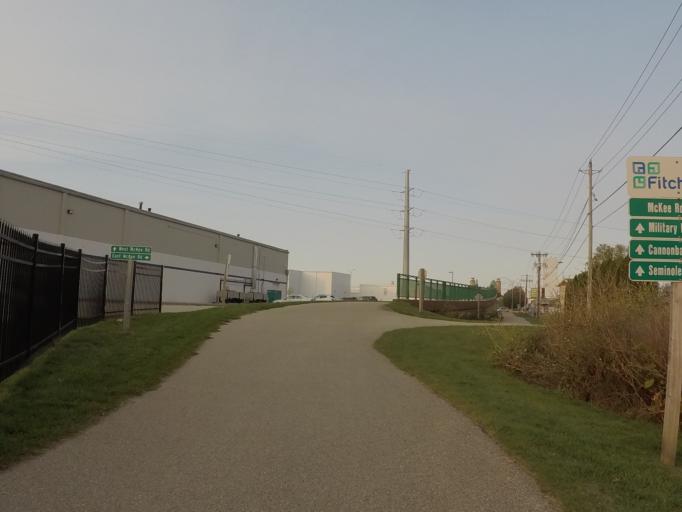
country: US
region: Wisconsin
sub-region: Dane County
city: Fitchburg
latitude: 43.0139
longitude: -89.4715
